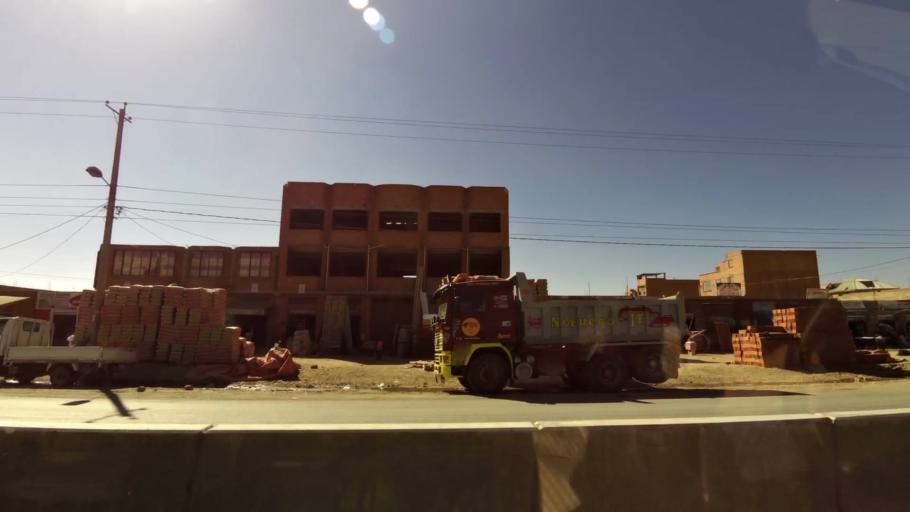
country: BO
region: La Paz
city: La Paz
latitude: -16.6164
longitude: -68.1826
